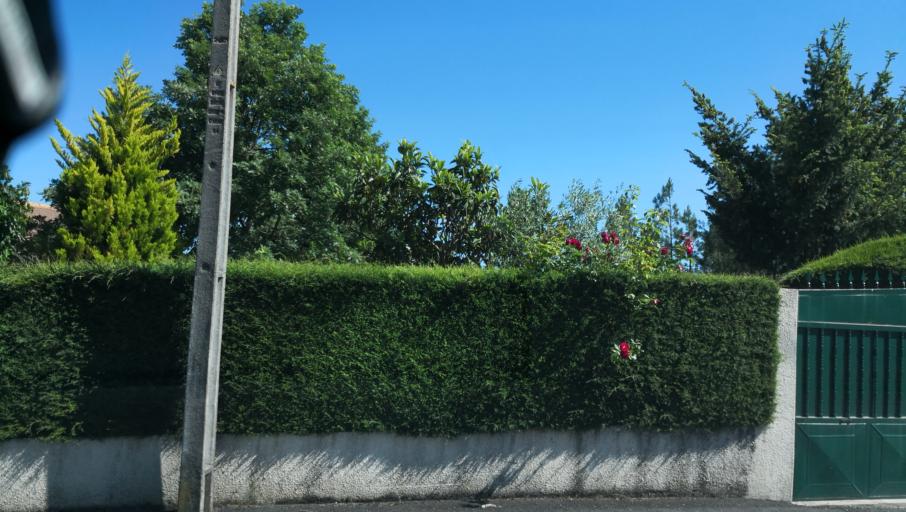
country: PT
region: Vila Real
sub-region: Vila Real
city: Vila Real
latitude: 41.2865
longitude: -7.6855
